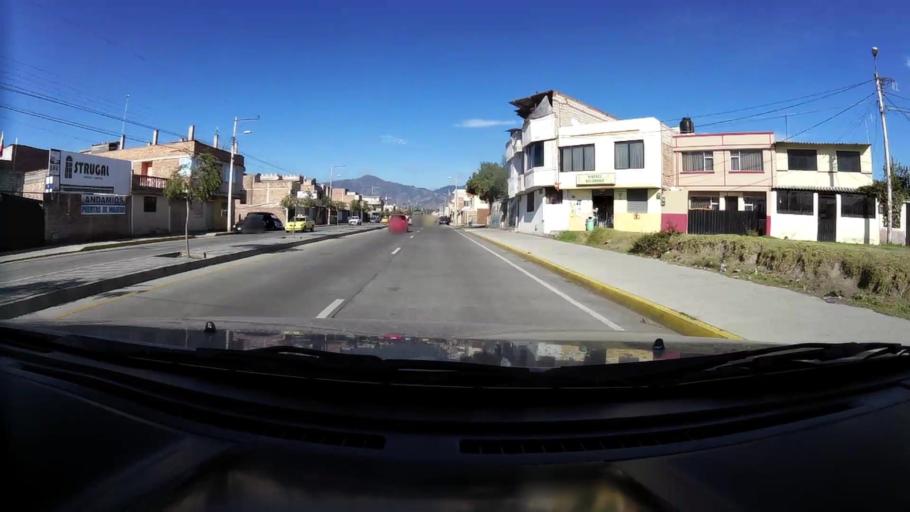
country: EC
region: Chimborazo
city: Riobamba
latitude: -1.6856
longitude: -78.6471
